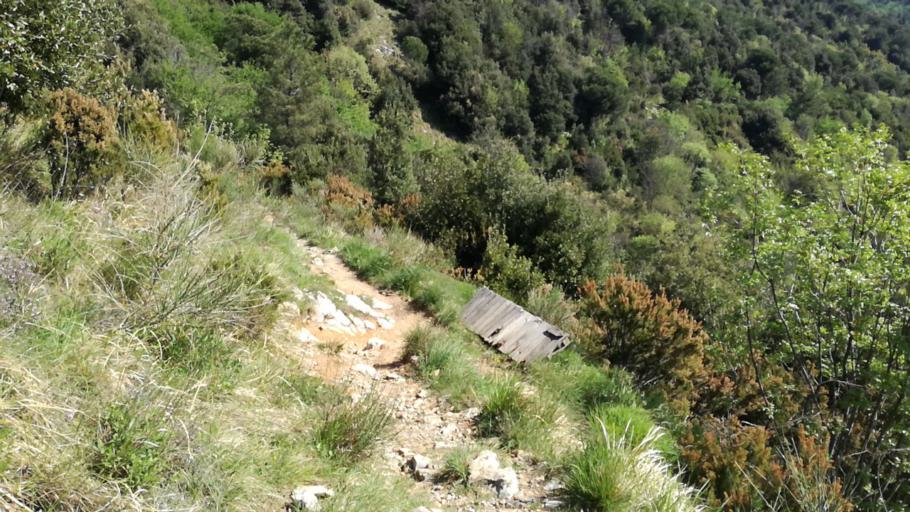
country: IT
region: Liguria
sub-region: Provincia di Genova
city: Genoa
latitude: 44.4337
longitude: 8.9190
